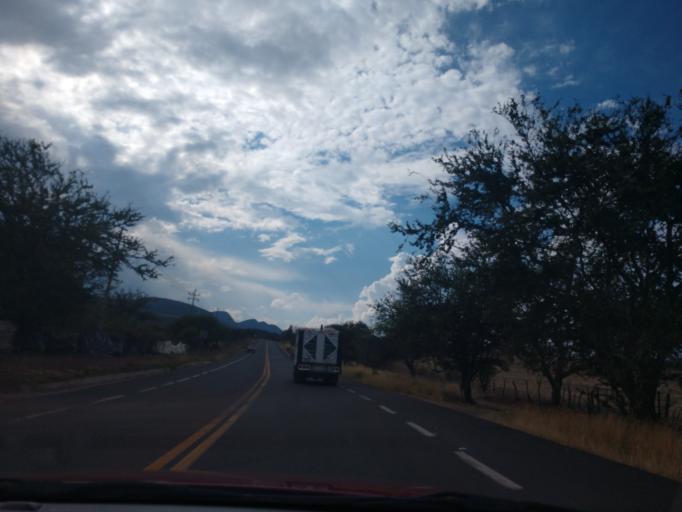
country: MX
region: Jalisco
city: Chapala
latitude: 20.1546
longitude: -103.1891
